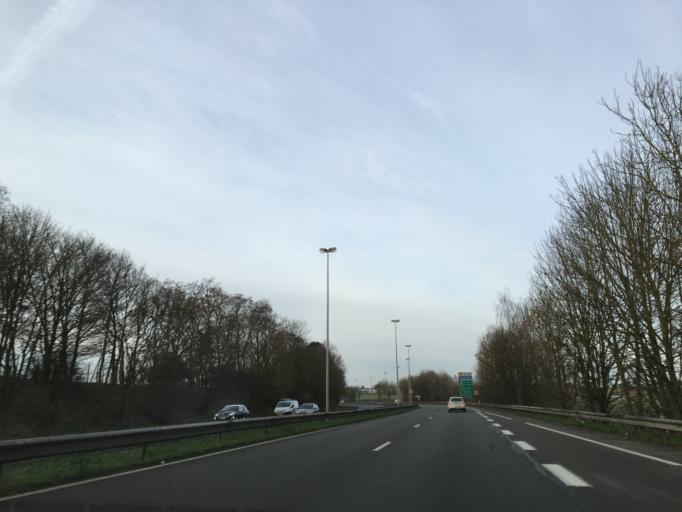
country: FR
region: Nord-Pas-de-Calais
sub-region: Departement du Pas-de-Calais
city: Saint-Nicolas
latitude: 50.3086
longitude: 2.7959
